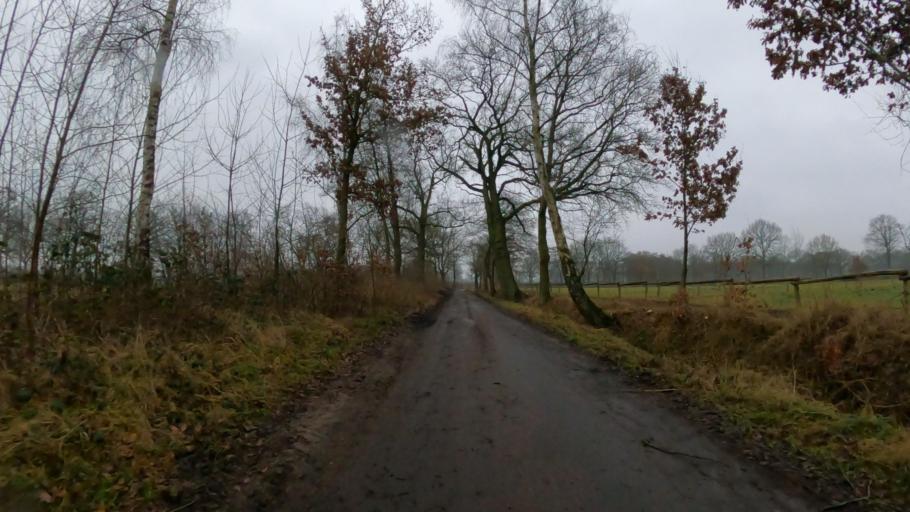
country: DE
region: Schleswig-Holstein
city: Rellingen
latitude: 53.5960
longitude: 9.7751
